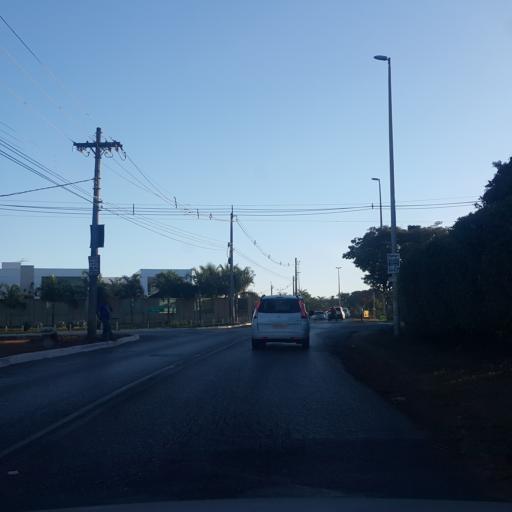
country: BR
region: Federal District
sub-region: Brasilia
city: Brasilia
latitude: -15.8588
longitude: -47.9787
